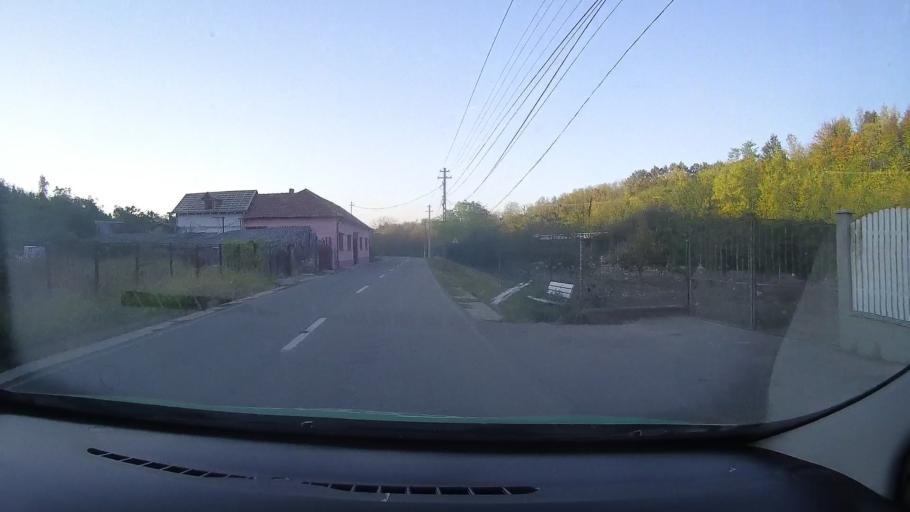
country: RO
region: Timis
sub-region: Comuna Traian Vuia
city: Traian Vuia
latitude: 45.7618
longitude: 22.0978
